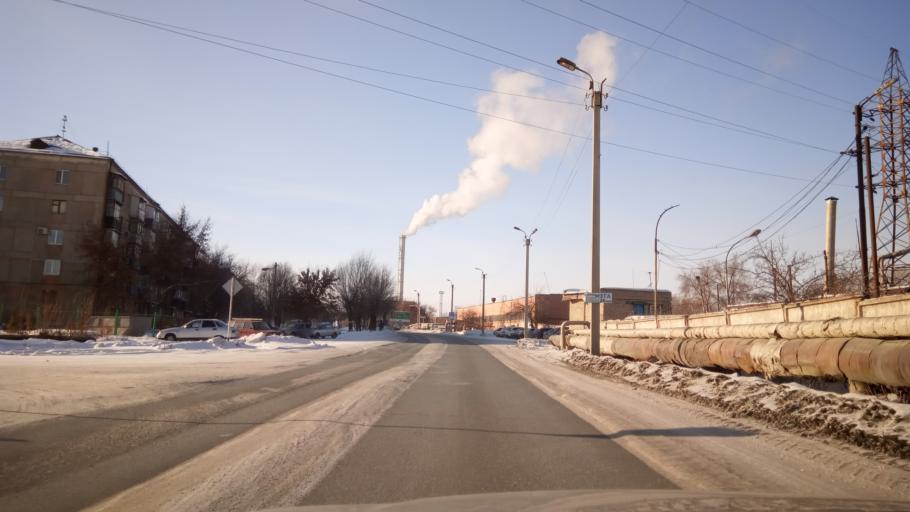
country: RU
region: Orenburg
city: Novotroitsk
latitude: 51.2001
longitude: 58.3134
